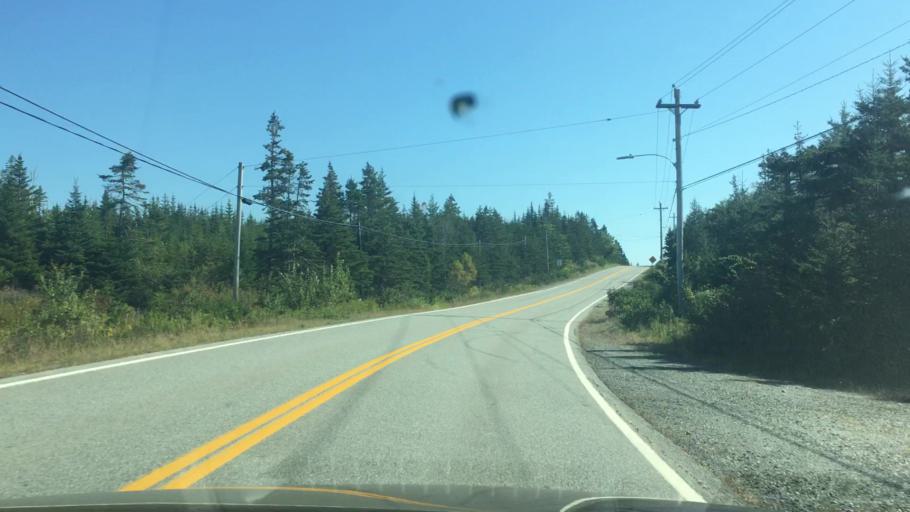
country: CA
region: Nova Scotia
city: New Glasgow
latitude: 44.8078
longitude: -62.6905
